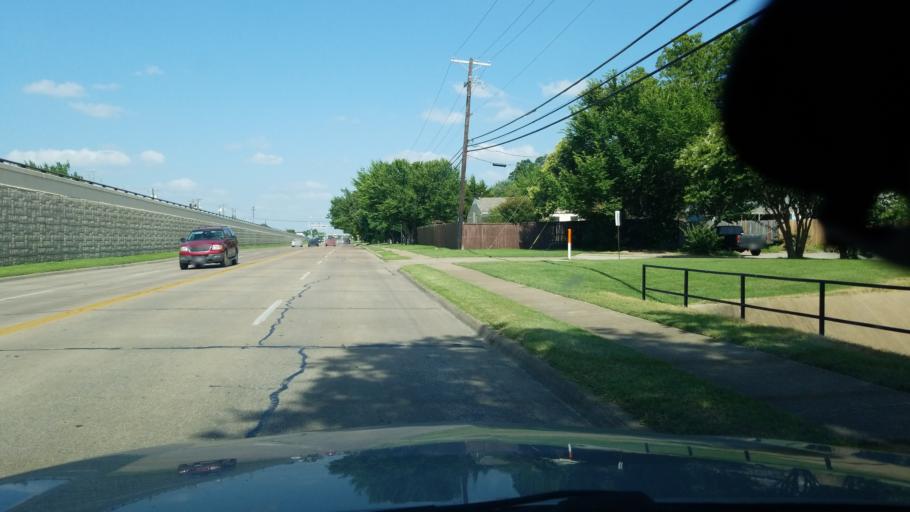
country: US
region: Texas
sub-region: Dallas County
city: Irving
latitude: 32.8152
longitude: -96.9712
